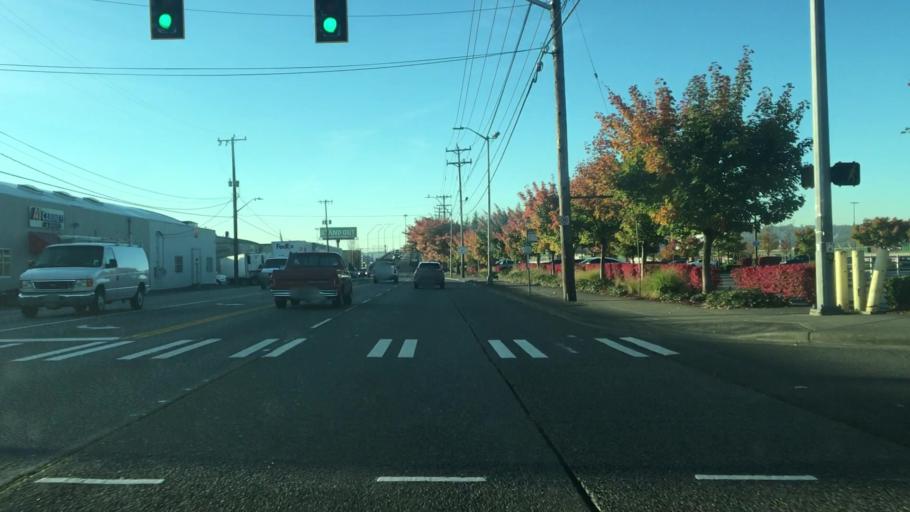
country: US
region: Washington
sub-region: King County
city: Seattle
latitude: 47.5646
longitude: -122.3295
